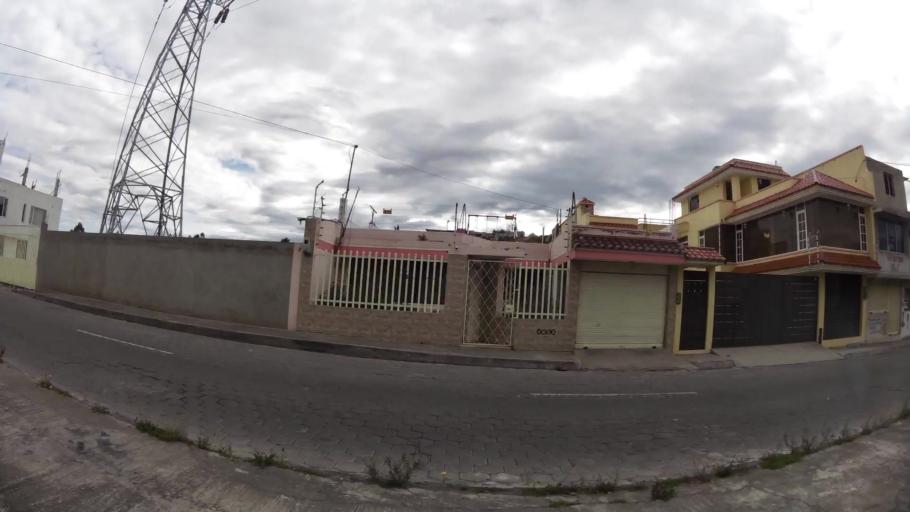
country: EC
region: Cotopaxi
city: Latacunga
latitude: -0.9379
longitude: -78.6230
